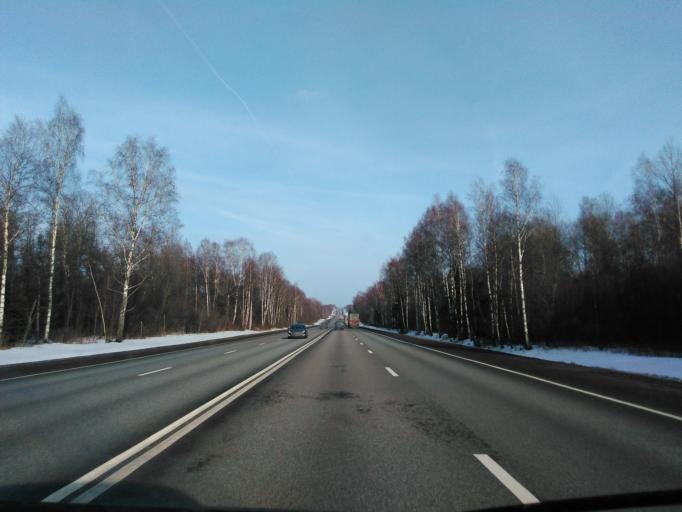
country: RU
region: Smolensk
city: Vyaz'ma
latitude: 55.1883
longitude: 34.0656
